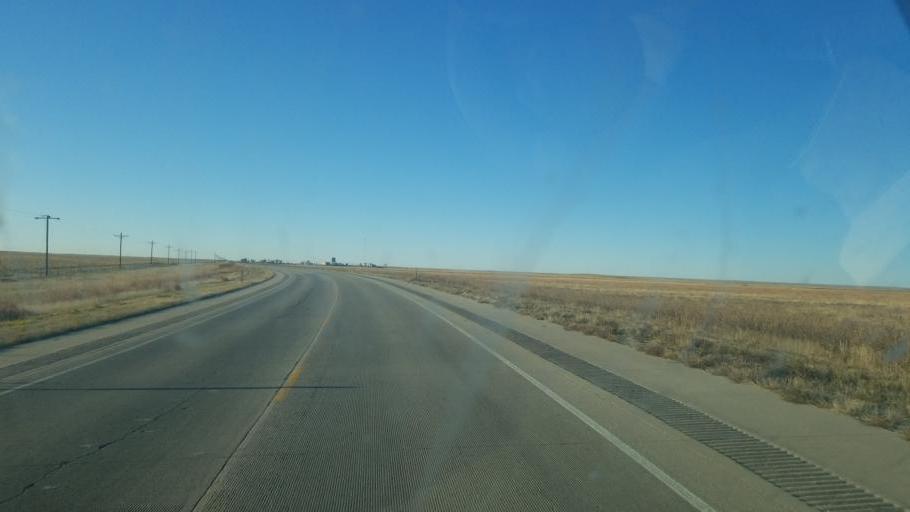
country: US
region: Colorado
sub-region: Kiowa County
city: Eads
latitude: 38.6787
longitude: -102.7857
